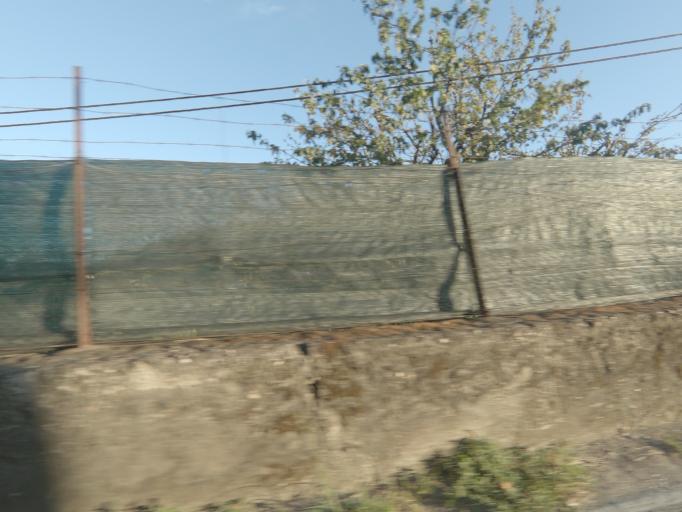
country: PT
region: Vila Real
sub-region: Mesao Frio
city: Mesao Frio
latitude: 41.1569
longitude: -7.8485
